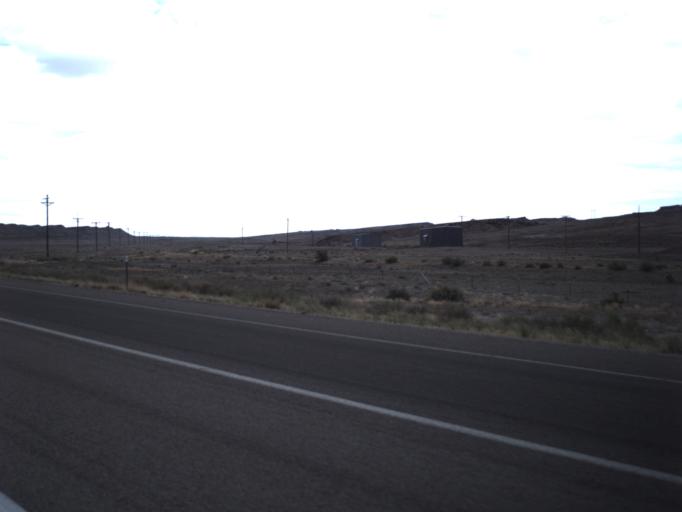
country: US
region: Utah
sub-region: Carbon County
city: East Carbon City
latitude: 38.9754
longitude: -110.1155
